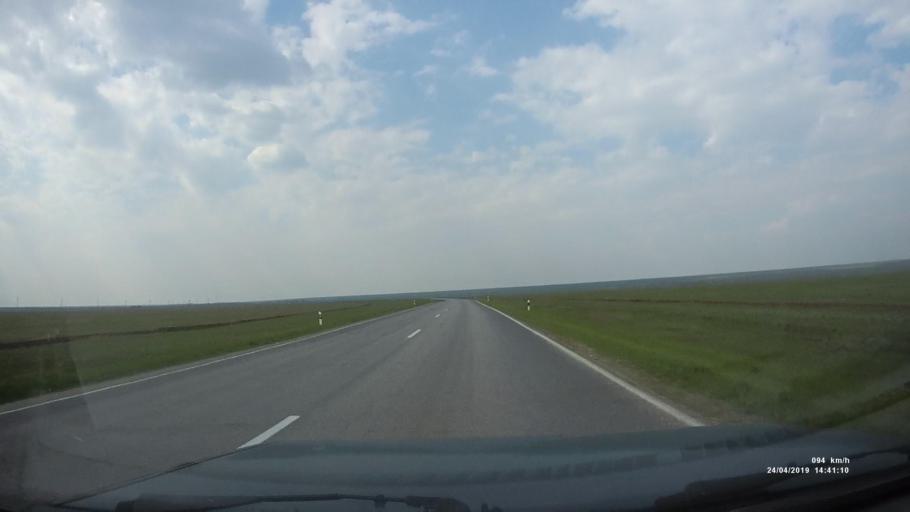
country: RU
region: Rostov
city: Remontnoye
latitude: 46.4422
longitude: 43.8829
